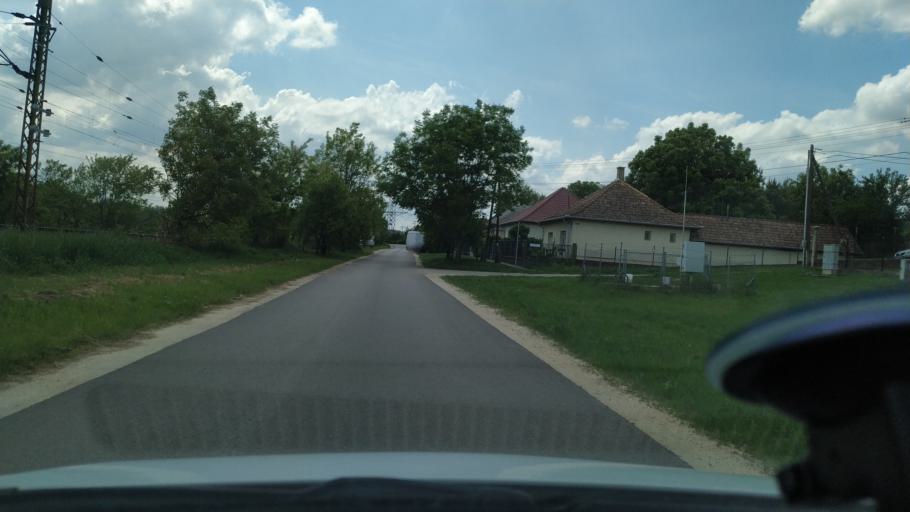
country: HU
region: Pest
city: Mende
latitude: 47.4383
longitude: 19.4638
